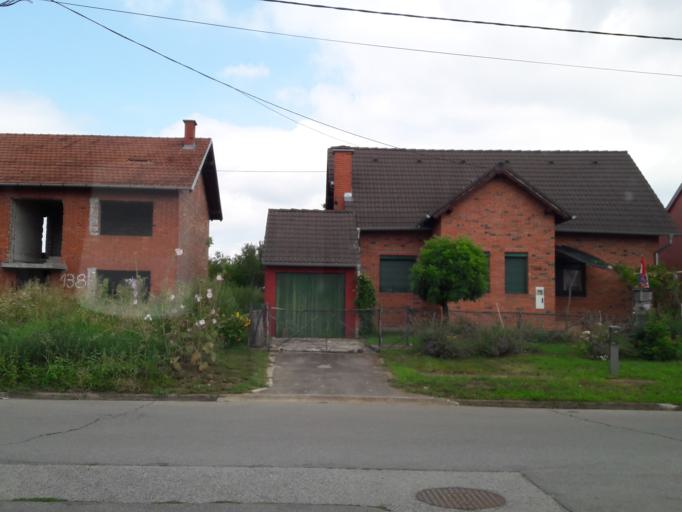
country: HR
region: Osjecko-Baranjska
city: Tenja
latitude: 45.5195
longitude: 18.7251
